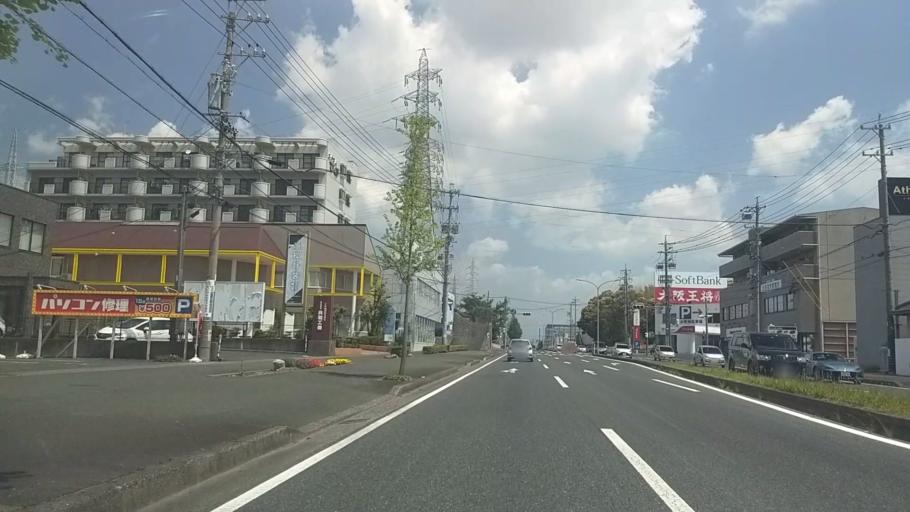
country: JP
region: Shizuoka
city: Hamamatsu
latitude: 34.7373
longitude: 137.7359
